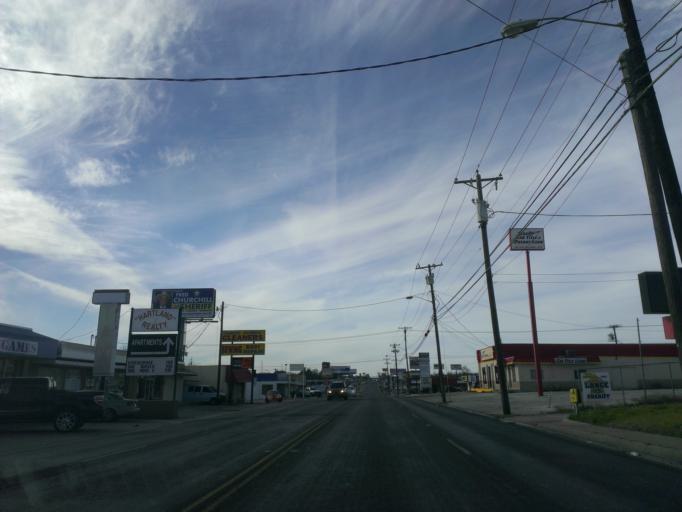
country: US
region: Texas
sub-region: Bell County
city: Killeen
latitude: 31.1266
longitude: -97.7287
